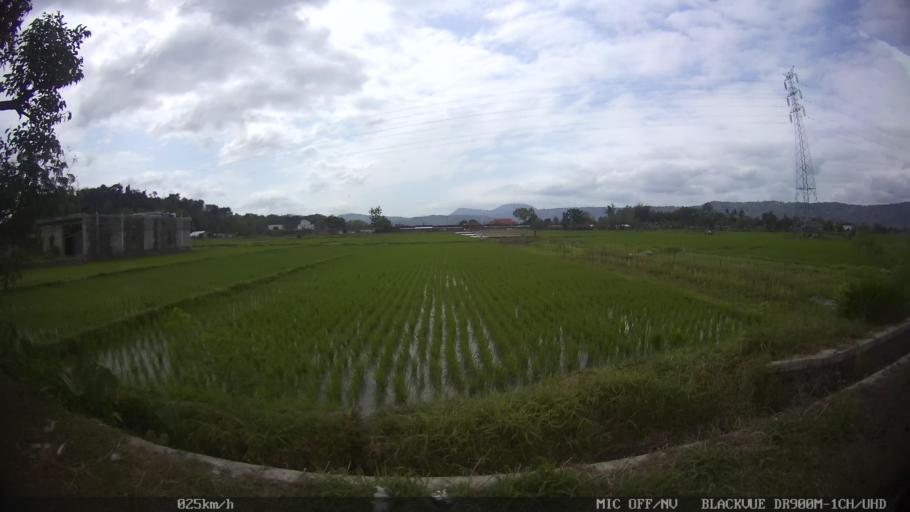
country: ID
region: Daerah Istimewa Yogyakarta
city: Depok
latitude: -7.8134
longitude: 110.4655
